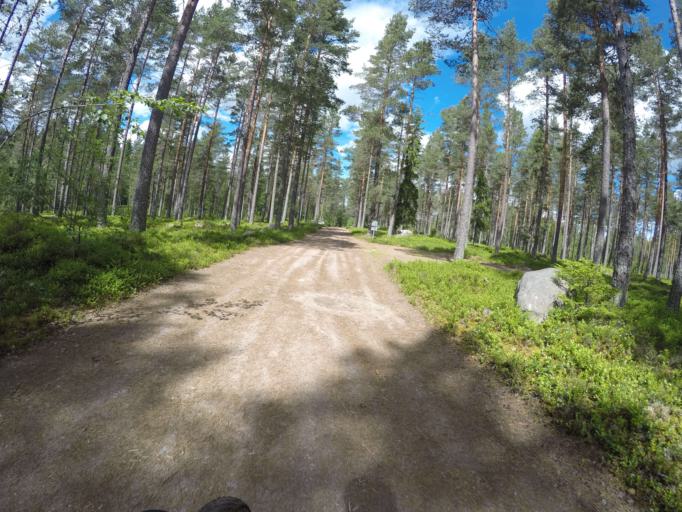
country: SE
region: Vaermland
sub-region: Filipstads Kommun
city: Lesjofors
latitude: 60.1425
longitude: 14.2723
